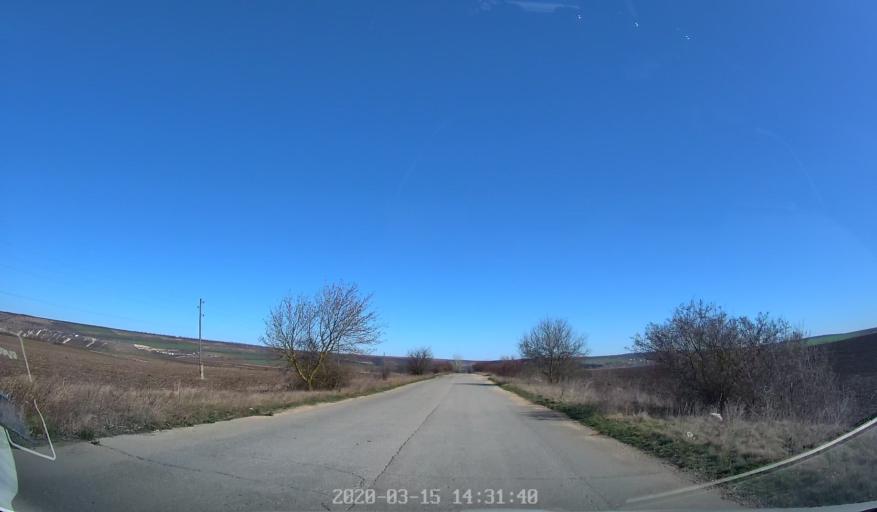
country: MD
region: Orhei
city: Orhei
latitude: 47.3442
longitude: 28.8989
